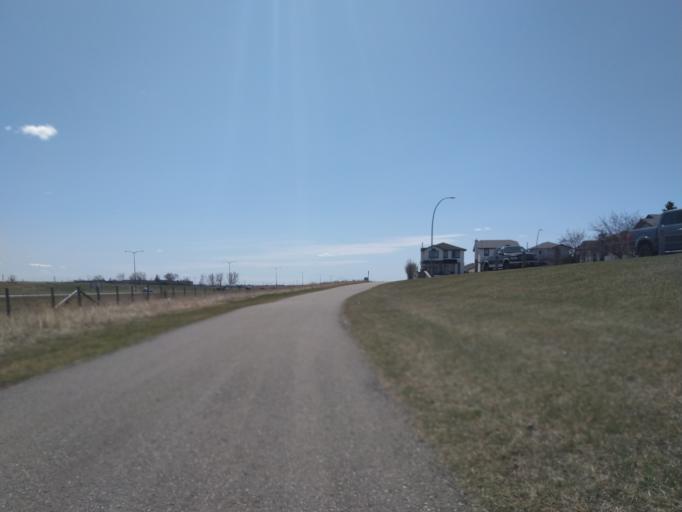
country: CA
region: Alberta
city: Chestermere
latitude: 51.0494
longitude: -113.9230
